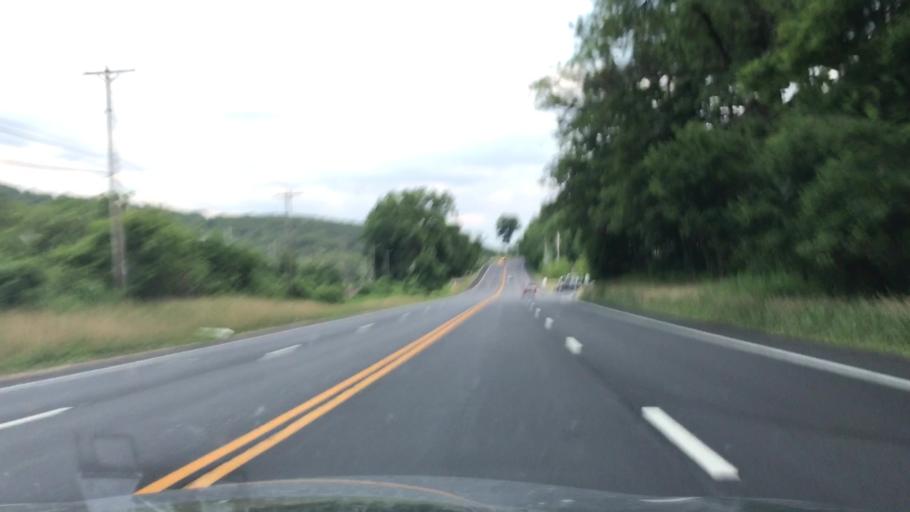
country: US
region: New York
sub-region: Rockland County
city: Sloatsburg
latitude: 41.2167
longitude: -74.1850
